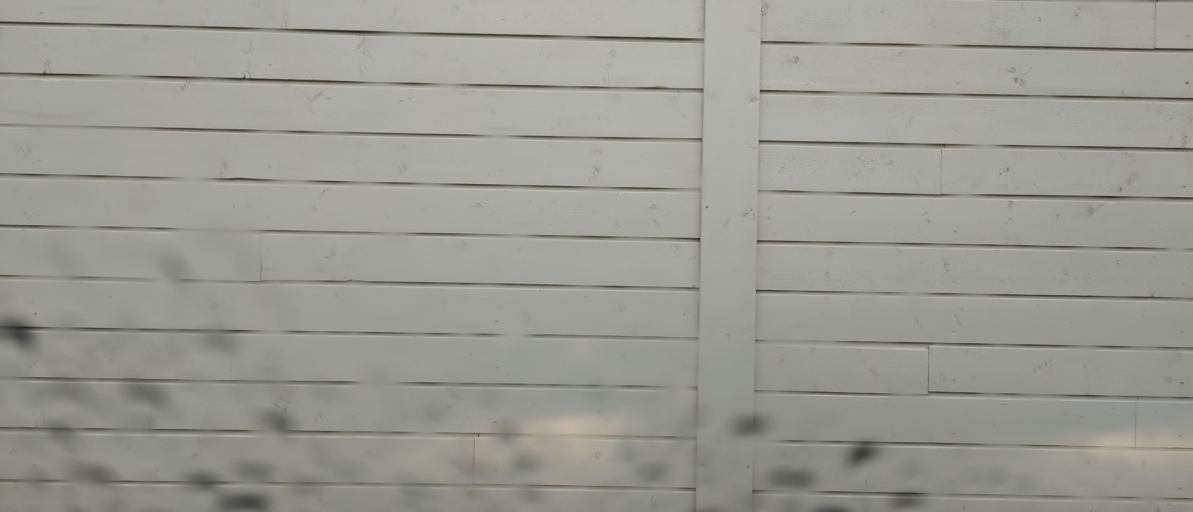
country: NO
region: More og Romsdal
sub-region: Kristiansund
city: Rensvik
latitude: 63.0108
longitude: 7.9757
